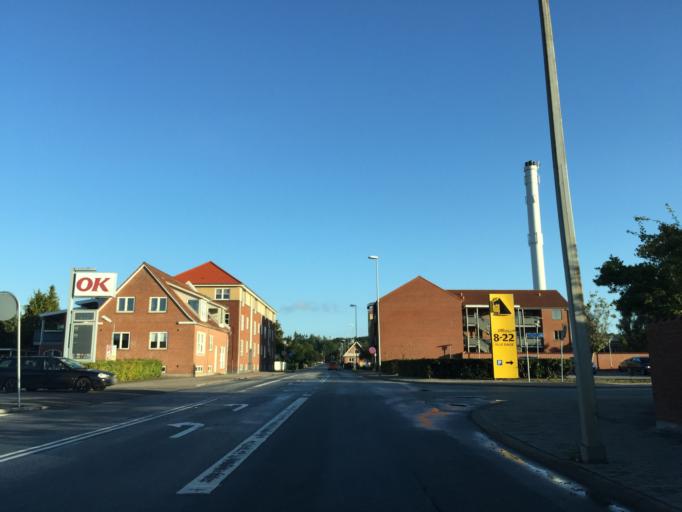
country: DK
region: Central Jutland
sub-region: Viborg Kommune
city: Bjerringbro
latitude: 56.3756
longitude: 9.6548
